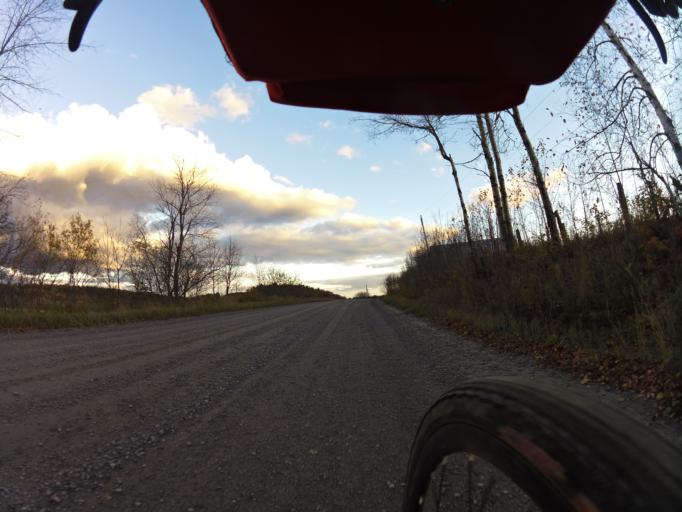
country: CA
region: Quebec
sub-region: Outaouais
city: Shawville
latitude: 45.6304
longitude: -76.3125
